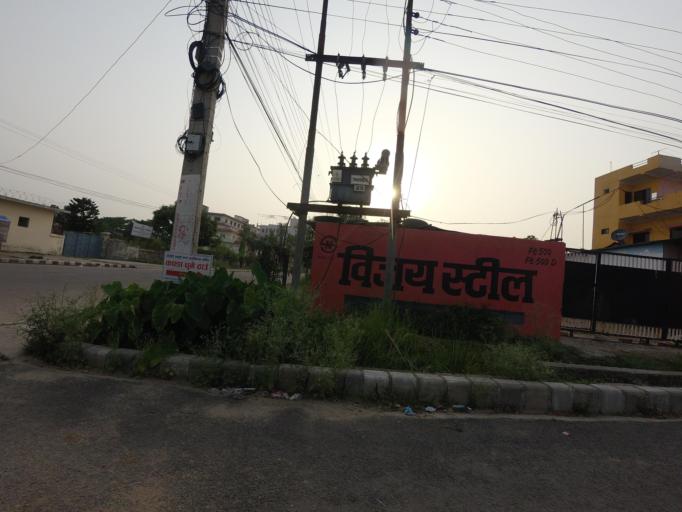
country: NP
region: Western Region
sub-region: Lumbini Zone
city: Bhairahawa
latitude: 27.5114
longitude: 83.4607
